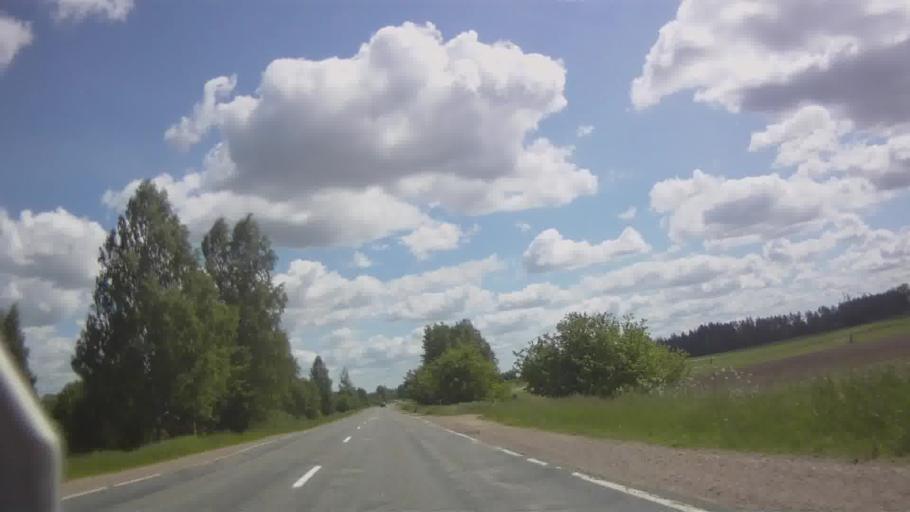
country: LV
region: Varaklani
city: Varaklani
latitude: 56.6129
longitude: 26.8267
